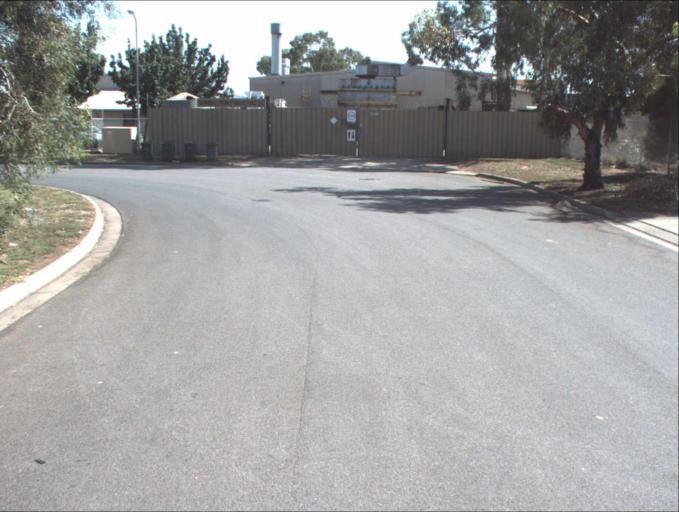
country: AU
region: South Australia
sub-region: Prospect
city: Prospect
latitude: -34.8812
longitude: 138.5810
